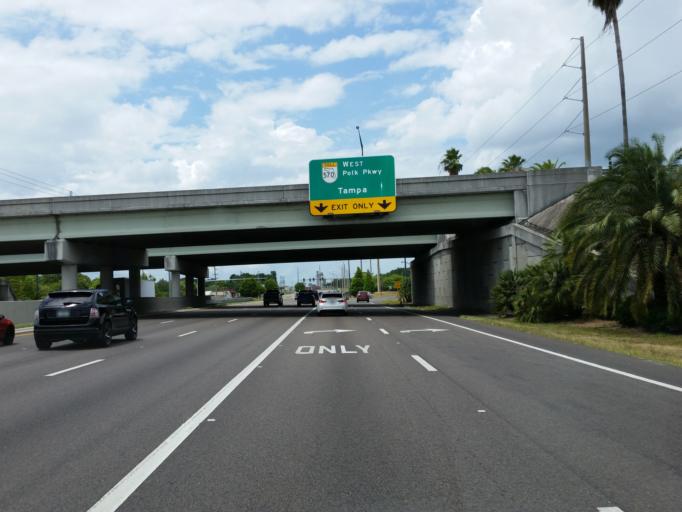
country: US
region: Florida
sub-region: Polk County
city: Crystal Lake
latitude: 27.9999
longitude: -81.9012
